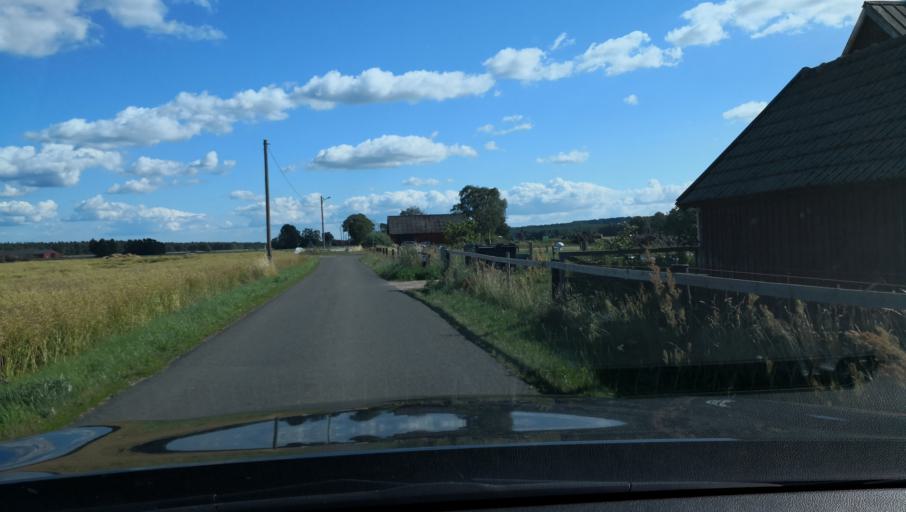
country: SE
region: Skane
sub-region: Kristianstads Kommun
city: Degeberga
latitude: 55.8146
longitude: 14.1889
